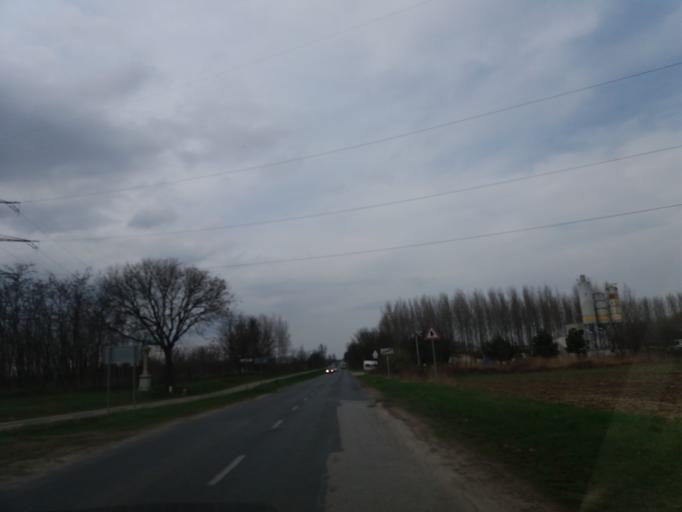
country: HU
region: Szabolcs-Szatmar-Bereg
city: Anarcs
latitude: 48.1872
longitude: 22.1018
